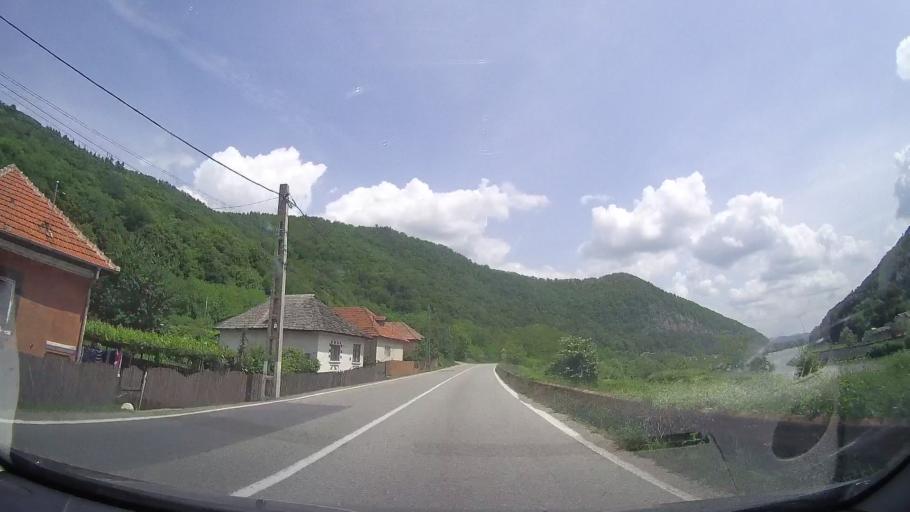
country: RO
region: Valcea
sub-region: Oras Calimanesti
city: Jiblea Veche
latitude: 45.2609
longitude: 24.3307
